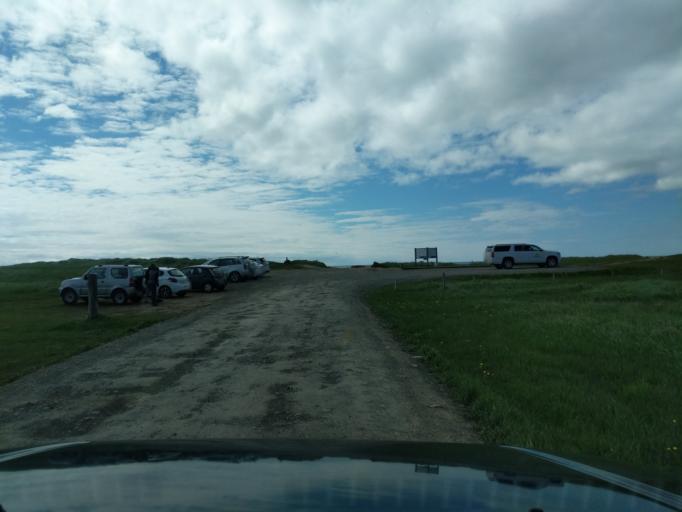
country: IS
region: West
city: Stykkisholmur
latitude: 64.8041
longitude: -23.0806
